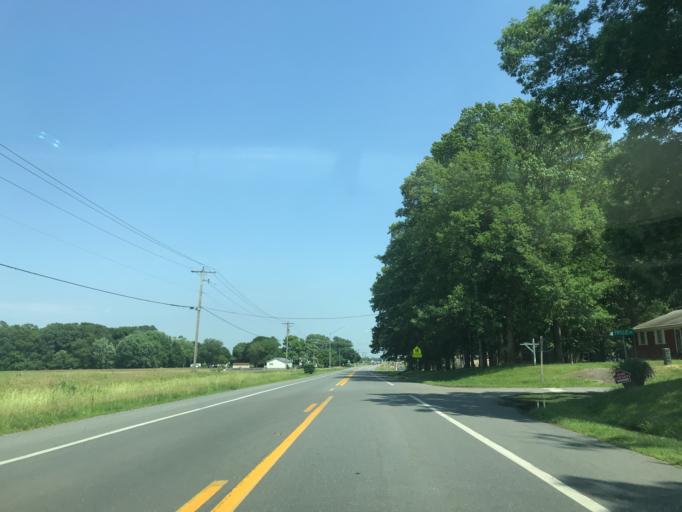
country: US
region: Maryland
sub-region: Dorchester County
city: Hurlock
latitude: 38.5900
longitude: -75.8755
